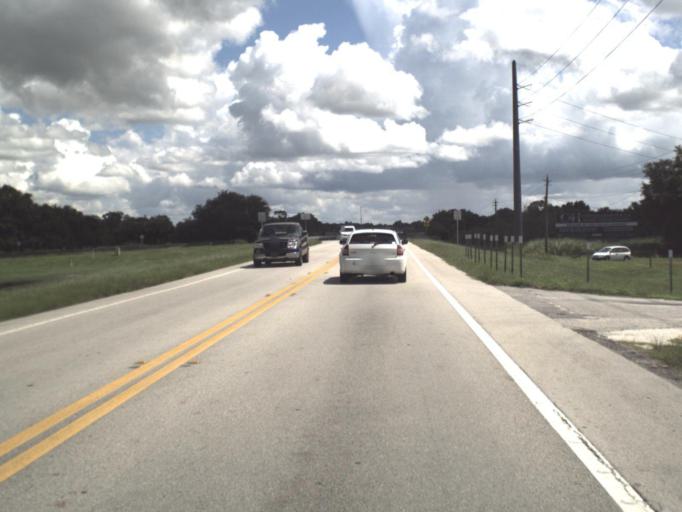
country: US
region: Florida
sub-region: DeSoto County
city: Arcadia
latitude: 27.2243
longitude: -81.8858
